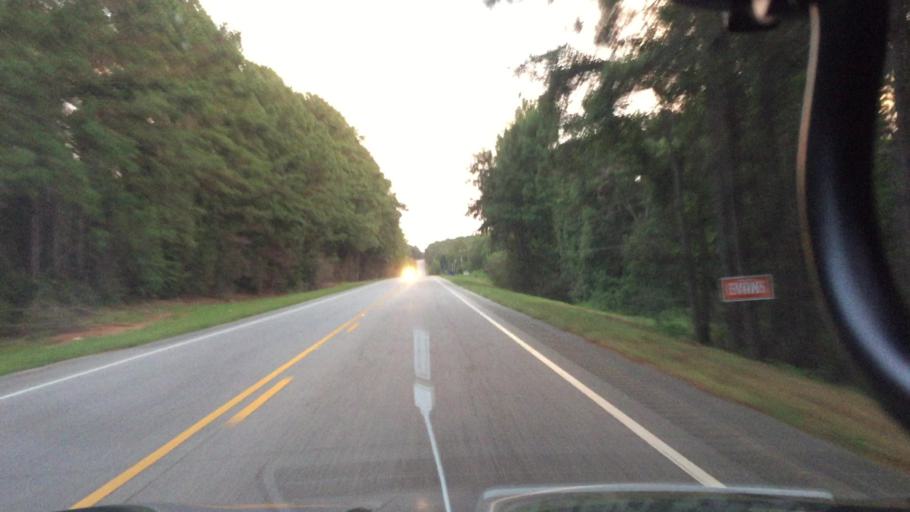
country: US
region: Alabama
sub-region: Coffee County
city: New Brockton
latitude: 31.3902
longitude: -85.8769
